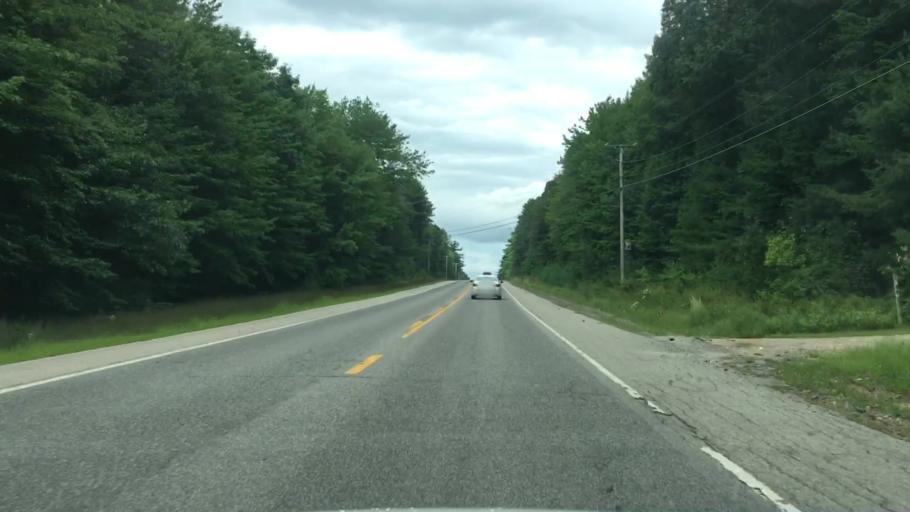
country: US
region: Maine
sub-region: York County
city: South Sanford
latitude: 43.3635
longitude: -70.7305
